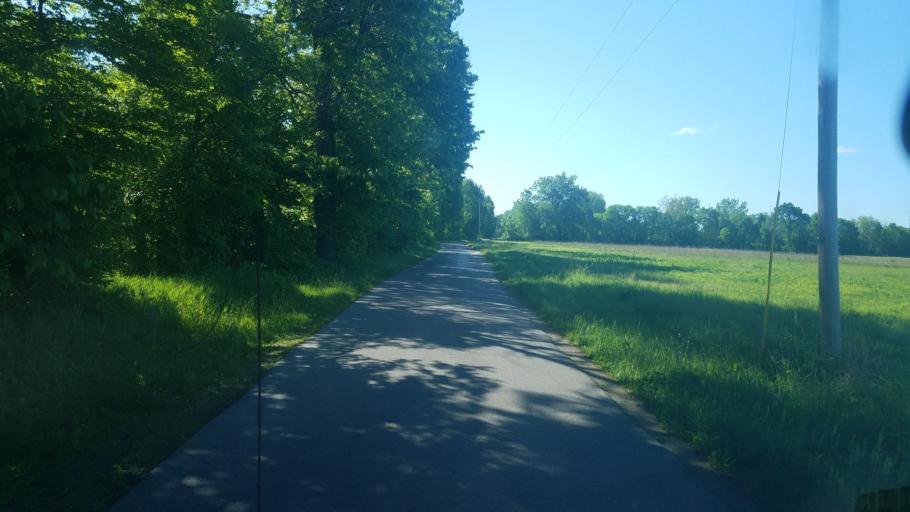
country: US
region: Ohio
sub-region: Marion County
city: Prospect
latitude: 40.5342
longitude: -83.2160
